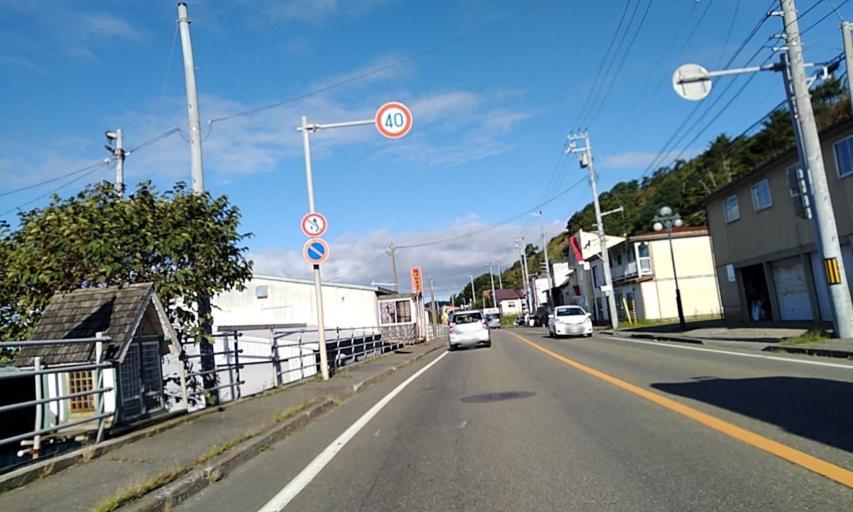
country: JP
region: Hokkaido
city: Shizunai-furukawacho
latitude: 42.1771
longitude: 142.7367
